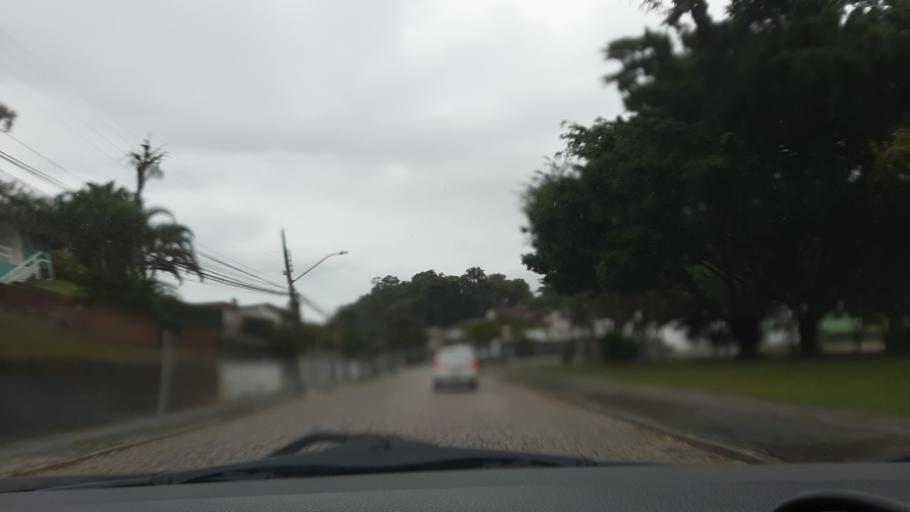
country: BR
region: Santa Catarina
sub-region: Joinville
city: Joinville
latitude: -26.3157
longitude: -48.8570
